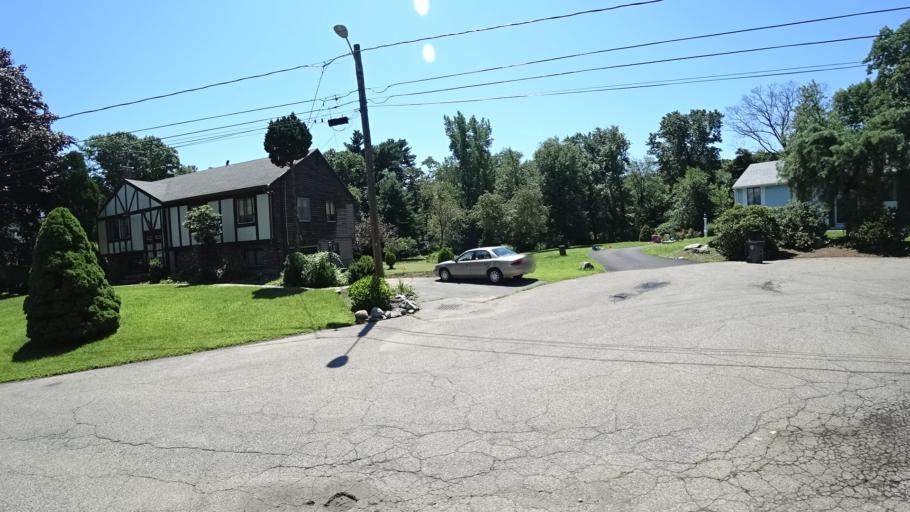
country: US
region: Massachusetts
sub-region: Norfolk County
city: Dedham
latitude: 42.2353
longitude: -71.1886
